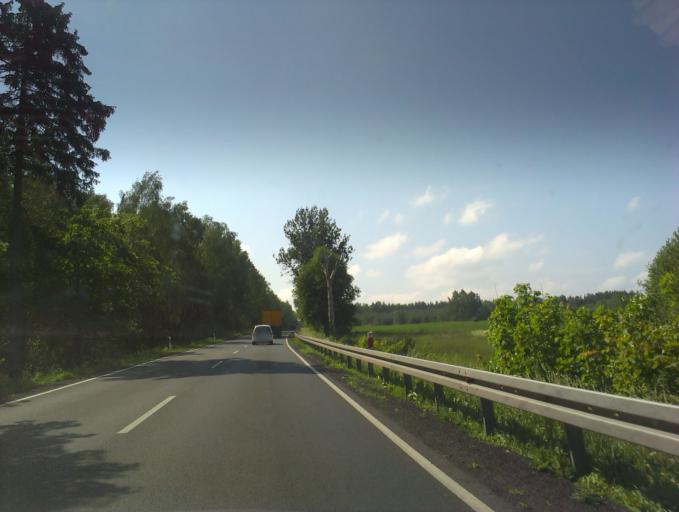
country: PL
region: Greater Poland Voivodeship
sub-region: Powiat zlotowski
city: Okonek
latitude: 53.5213
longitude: 16.8532
